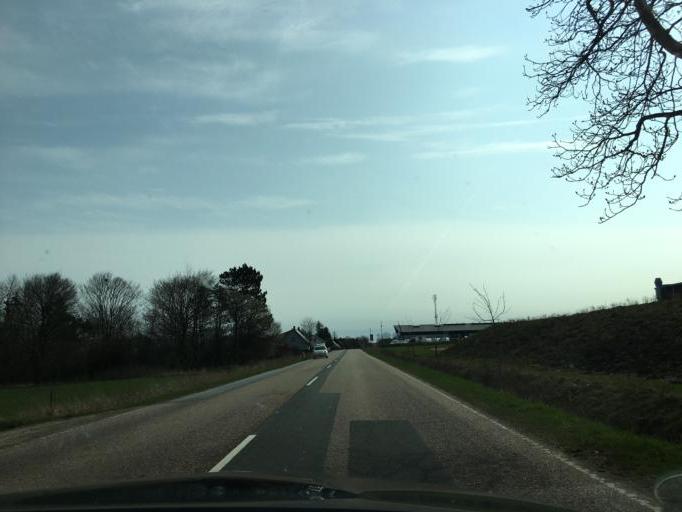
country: DK
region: South Denmark
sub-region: Vejen Kommune
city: Vejen
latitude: 55.4915
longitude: 9.1101
